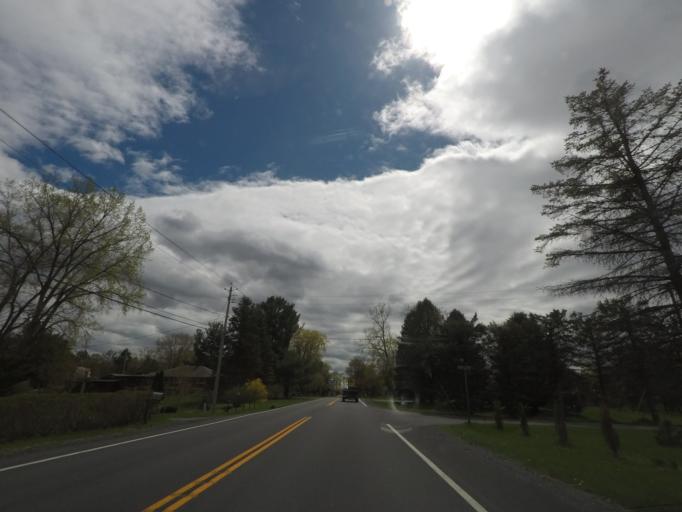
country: US
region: New York
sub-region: Rensselaer County
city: Castleton-on-Hudson
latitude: 42.5105
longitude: -73.7870
